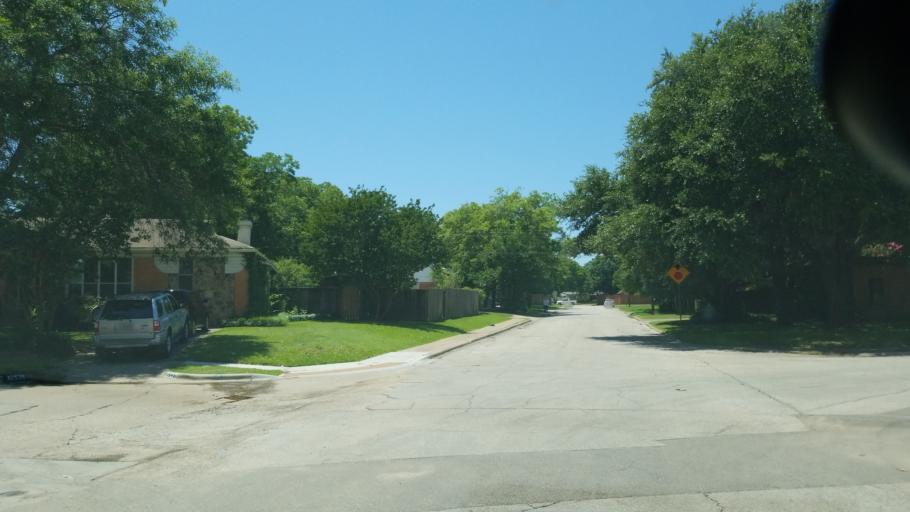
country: US
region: Texas
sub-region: Dallas County
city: Irving
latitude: 32.8312
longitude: -96.9706
